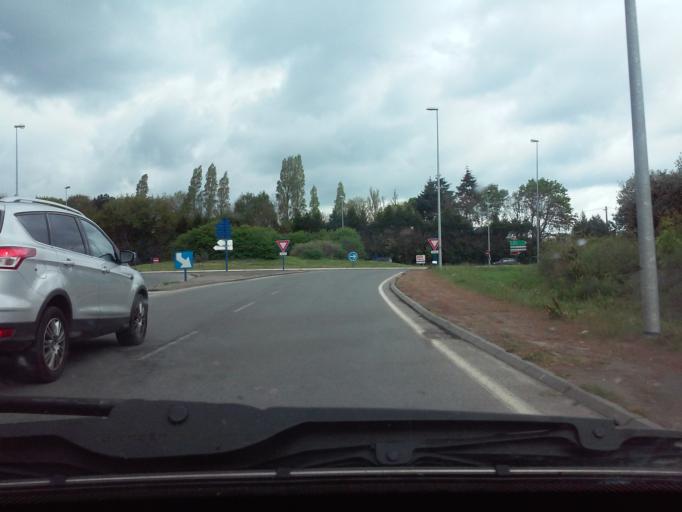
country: FR
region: Brittany
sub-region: Departement d'Ille-et-Vilaine
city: Dinard
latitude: 48.6106
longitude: -2.0681
